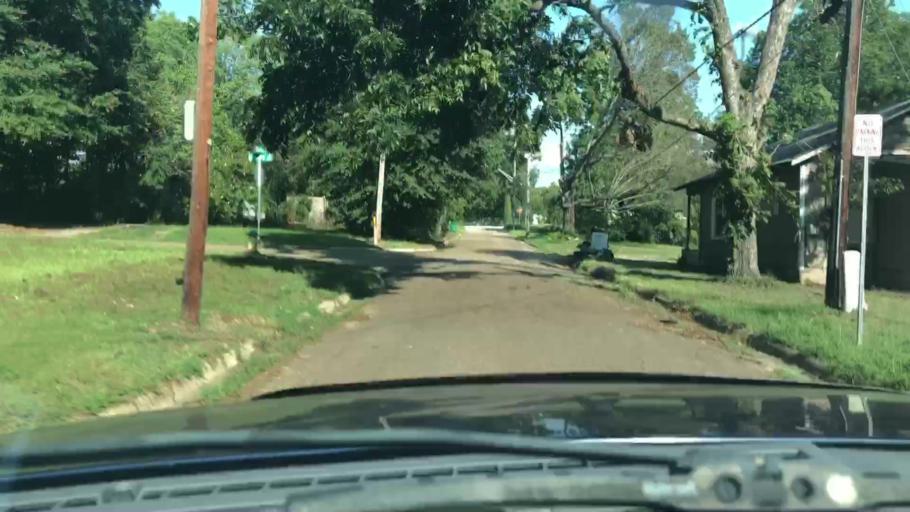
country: US
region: Texas
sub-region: Bowie County
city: Texarkana
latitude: 33.4167
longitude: -94.0625
